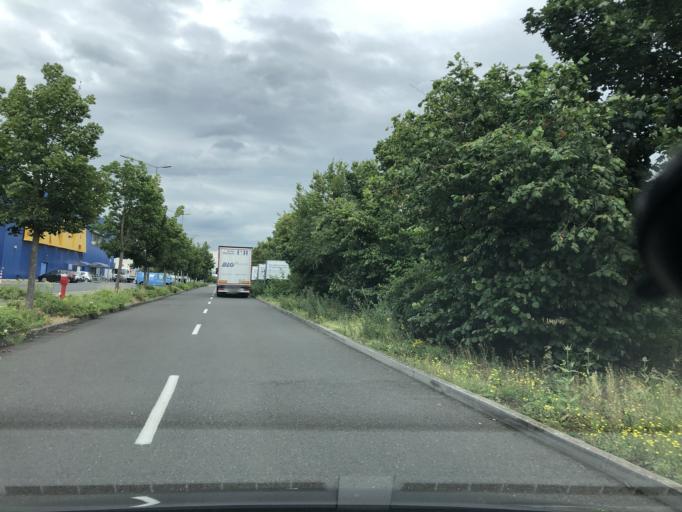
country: DE
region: Hesse
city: Lampertheim
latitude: 49.5547
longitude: 8.4432
